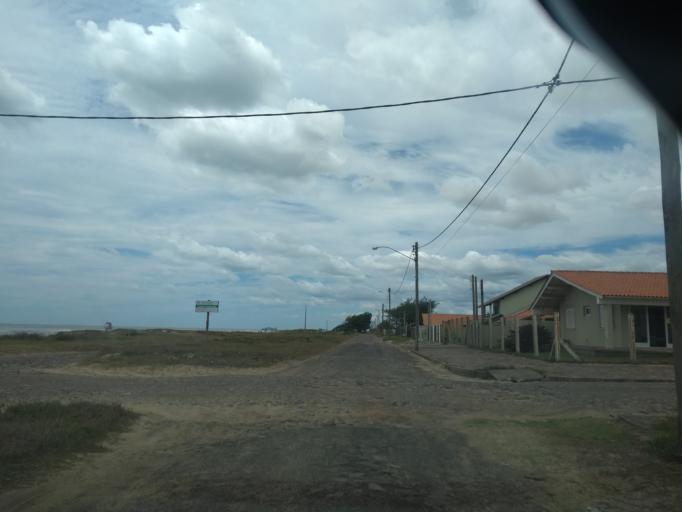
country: BR
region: Rio Grande do Sul
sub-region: Tramandai
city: Tramandai
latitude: -30.0659
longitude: -50.1591
